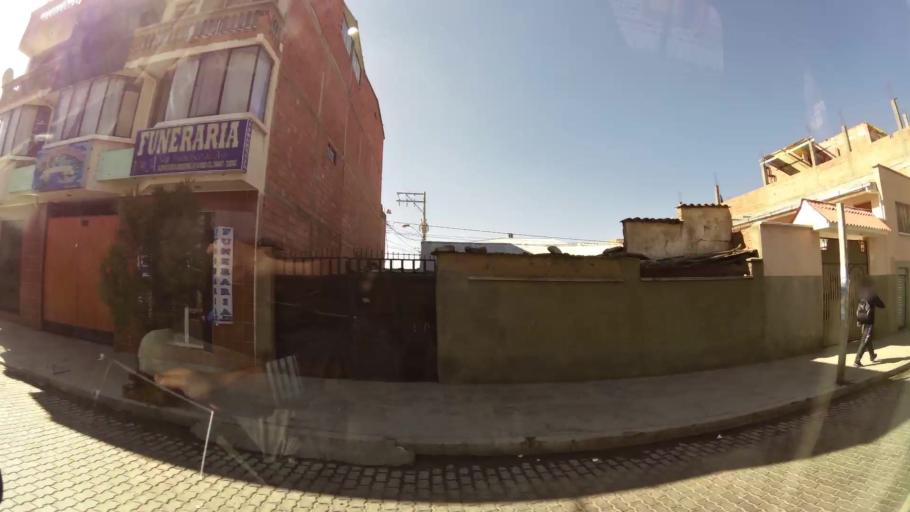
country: BO
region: La Paz
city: La Paz
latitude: -16.5214
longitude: -68.1526
